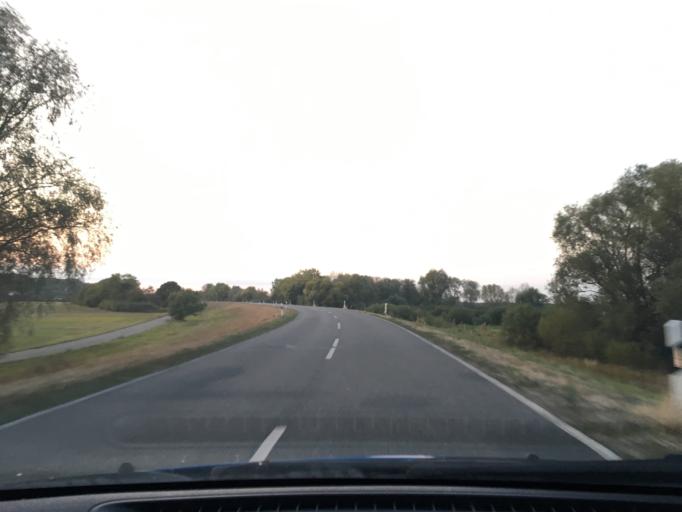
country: DE
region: Lower Saxony
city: Hitzacker
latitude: 53.1442
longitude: 11.0642
